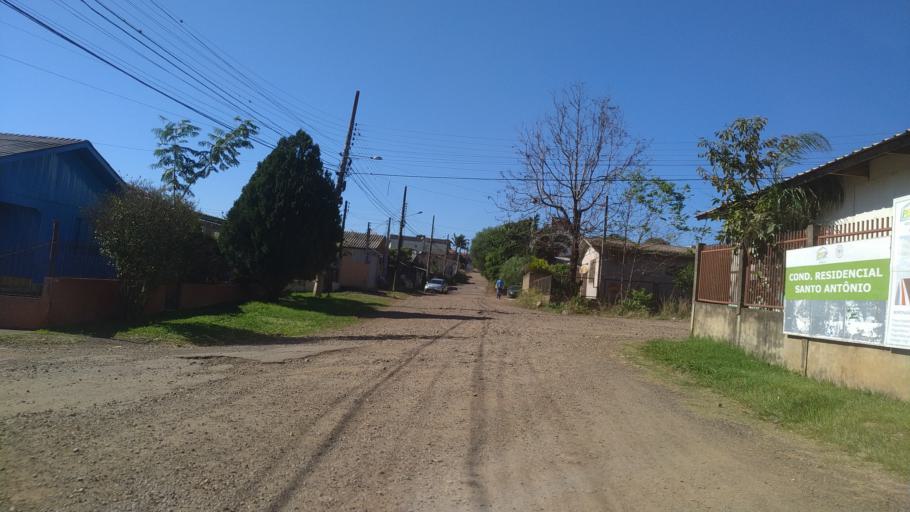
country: BR
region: Santa Catarina
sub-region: Chapeco
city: Chapeco
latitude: -27.1177
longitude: -52.6253
